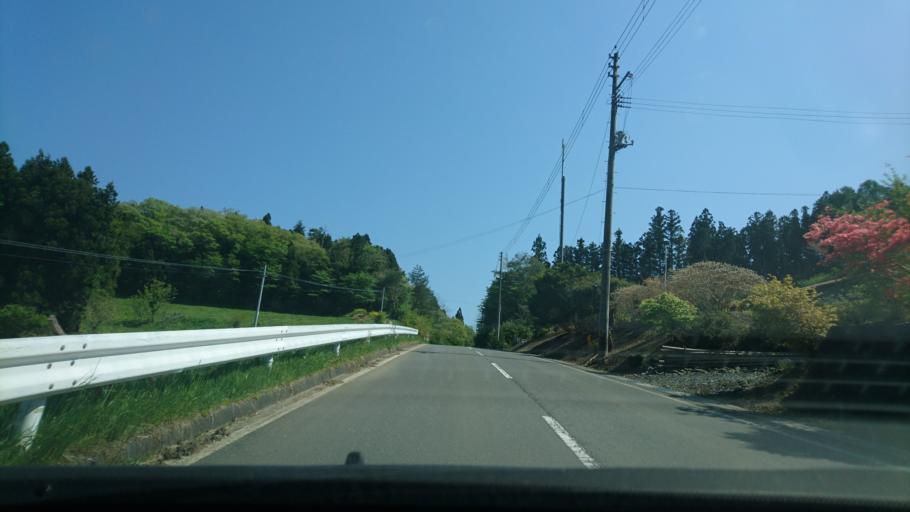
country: JP
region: Iwate
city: Ichinoseki
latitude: 38.9253
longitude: 141.2772
